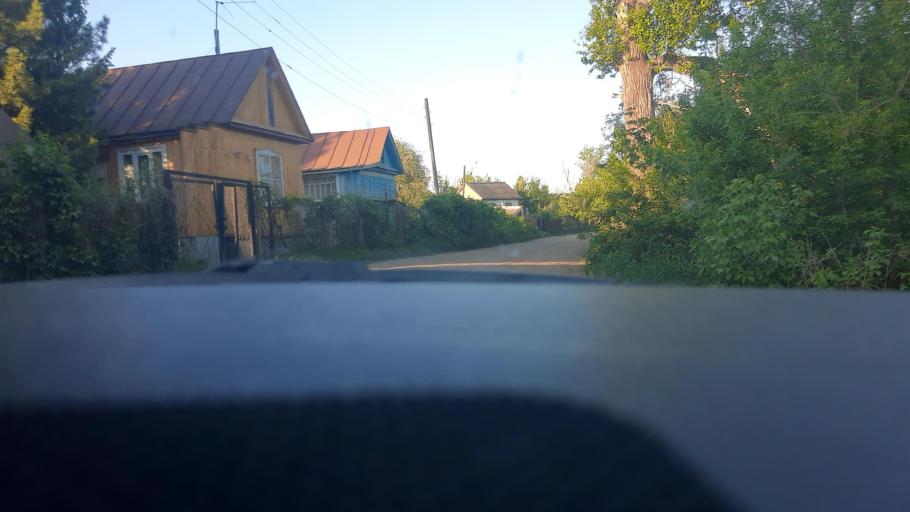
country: RU
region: Bashkortostan
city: Chishmy
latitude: 54.6337
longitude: 55.5362
